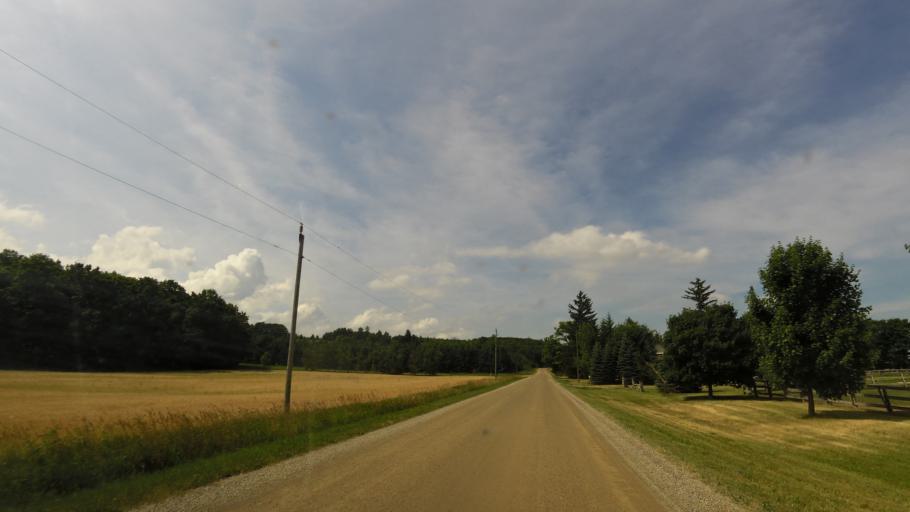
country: CA
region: Ontario
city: Orangeville
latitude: 44.0068
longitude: -80.0513
